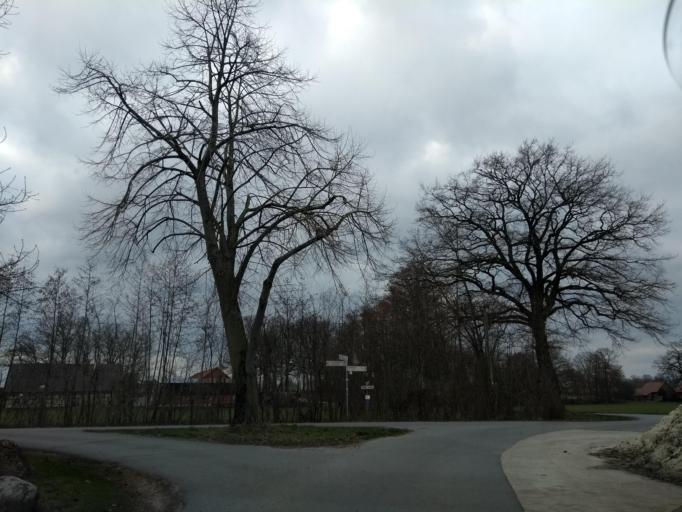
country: DE
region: North Rhine-Westphalia
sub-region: Regierungsbezirk Detmold
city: Delbruck
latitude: 51.7475
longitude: 8.4904
